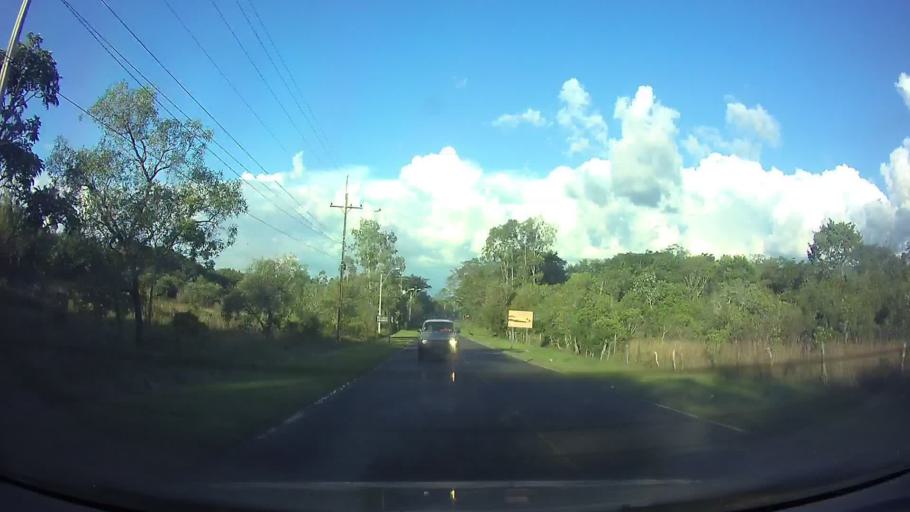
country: PY
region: Cordillera
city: Emboscada
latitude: -25.1949
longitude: -57.3169
